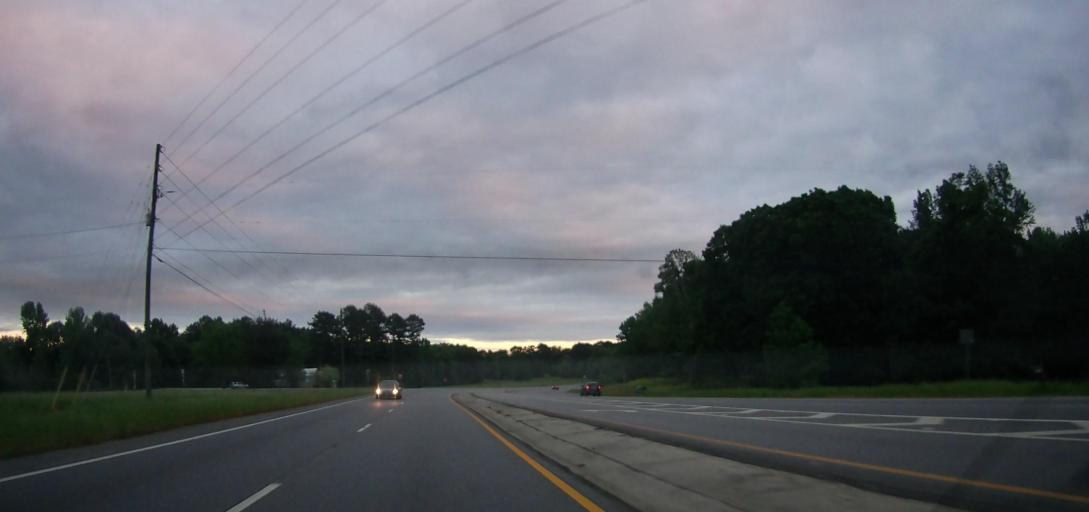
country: US
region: Georgia
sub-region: Jackson County
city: Arcade
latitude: 34.0482
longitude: -83.4976
